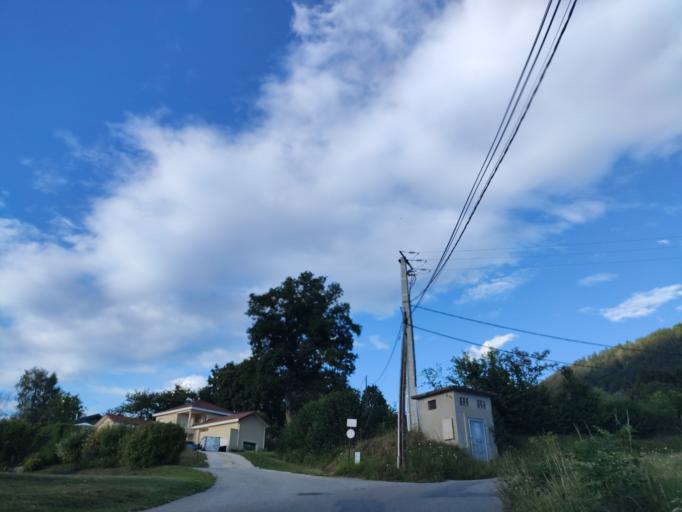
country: FR
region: Rhone-Alpes
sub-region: Departement de l'Isere
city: Revel
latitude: 45.1587
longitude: 5.8542
